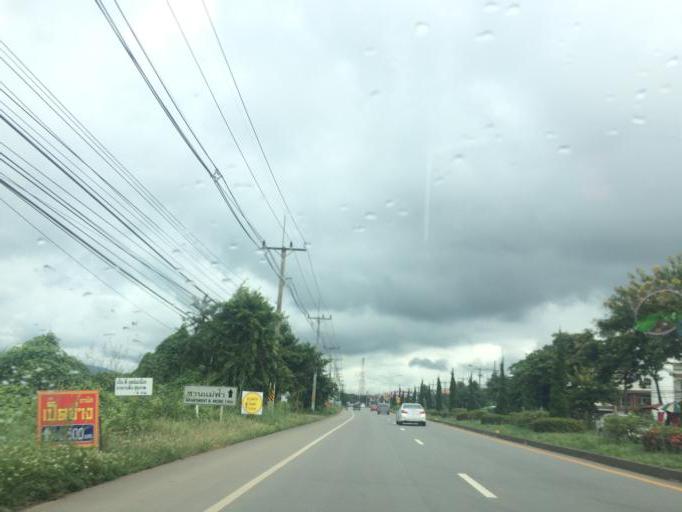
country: TH
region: Chiang Rai
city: Mae Chan
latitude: 20.0378
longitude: 99.8753
